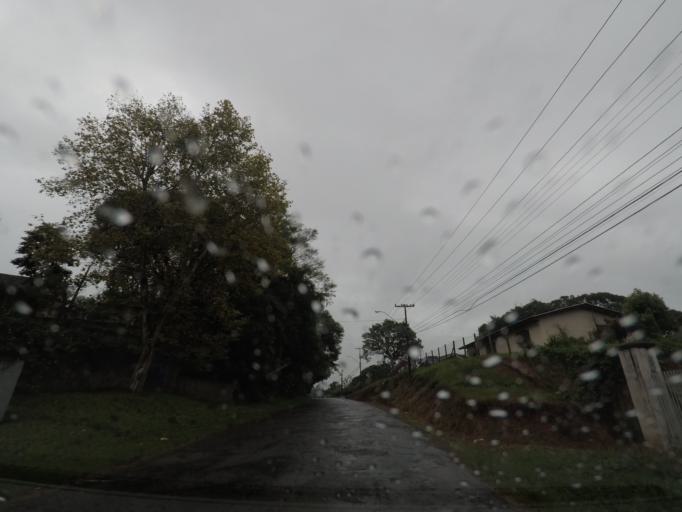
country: BR
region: Parana
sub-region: Campo Largo
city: Campo Largo
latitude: -25.4615
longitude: -49.4134
